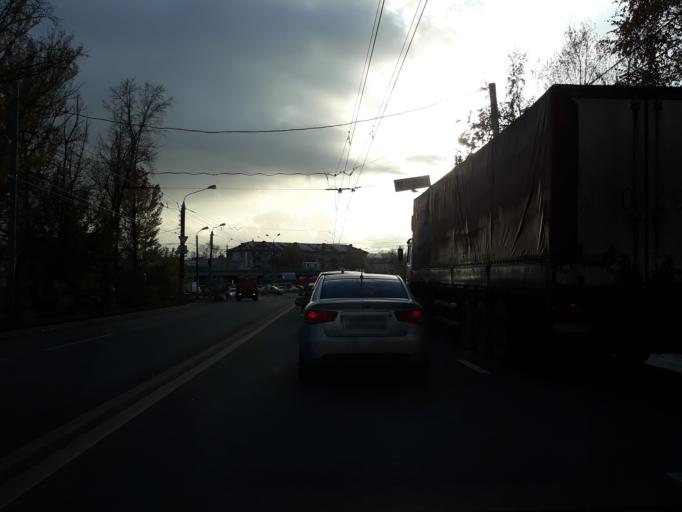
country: RU
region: Nizjnij Novgorod
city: Nizhniy Novgorod
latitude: 56.3164
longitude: 43.9007
